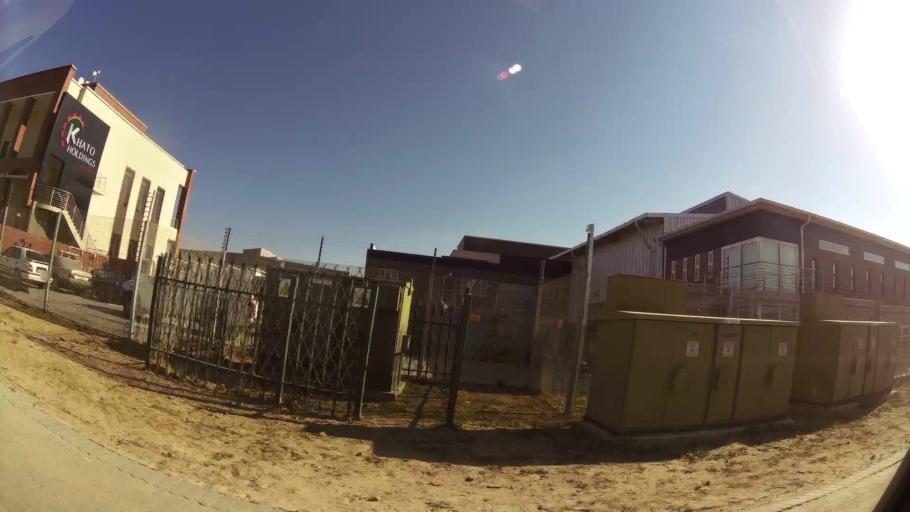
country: ZA
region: Gauteng
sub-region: City of Johannesburg Metropolitan Municipality
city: Midrand
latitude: -25.9189
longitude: 28.1261
